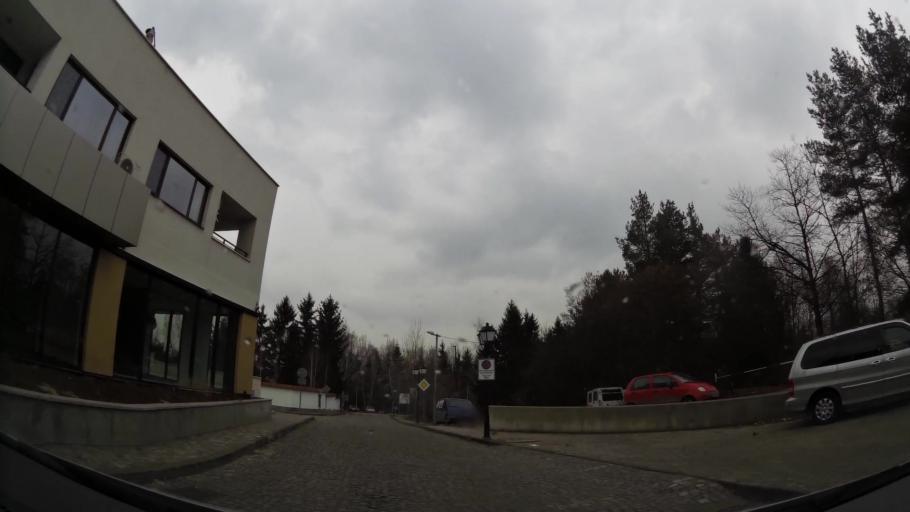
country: BG
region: Sofia-Capital
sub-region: Stolichna Obshtina
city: Sofia
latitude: 42.6158
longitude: 23.3763
